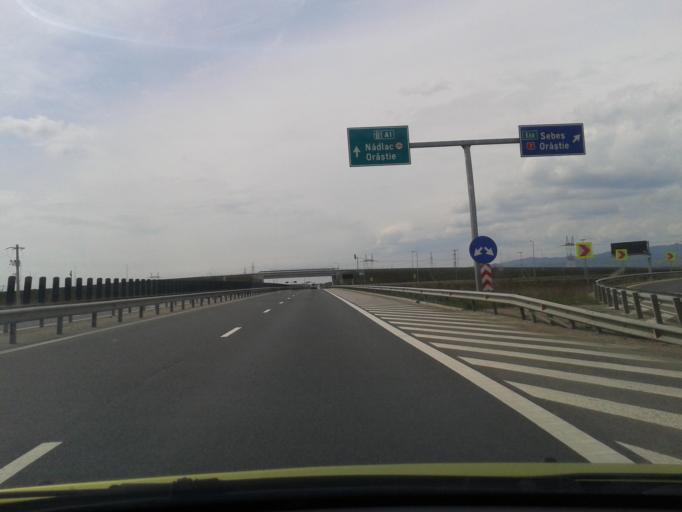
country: RO
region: Alba
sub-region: Municipiul Sebes
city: Lancram
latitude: 45.9788
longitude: 23.5279
